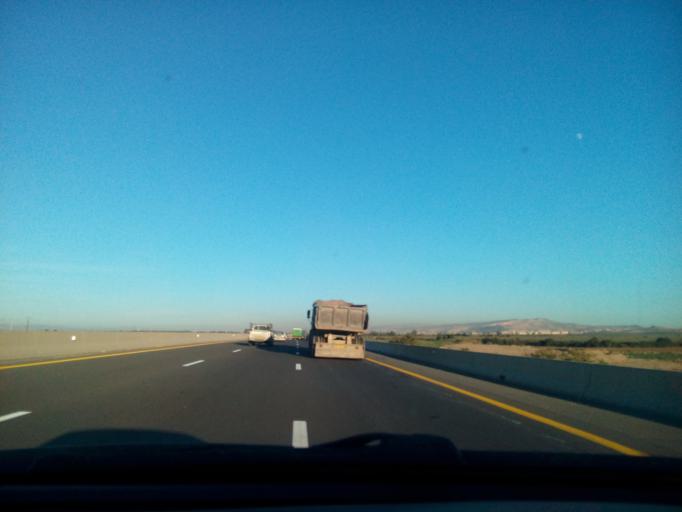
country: DZ
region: Relizane
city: Djidiouia
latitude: 35.9267
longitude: 0.7901
